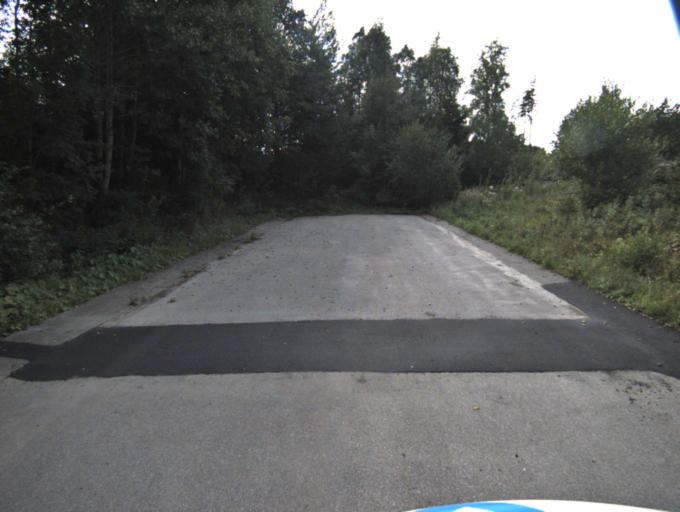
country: SE
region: Vaestra Goetaland
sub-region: Ulricehamns Kommun
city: Ulricehamn
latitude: 57.8336
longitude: 13.2711
